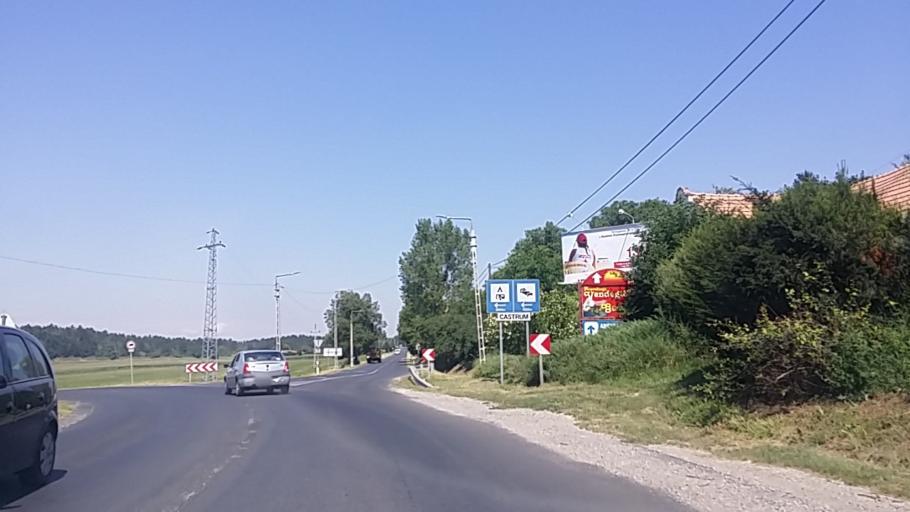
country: HU
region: Zala
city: Cserszegtomaj
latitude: 46.7911
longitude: 17.2116
